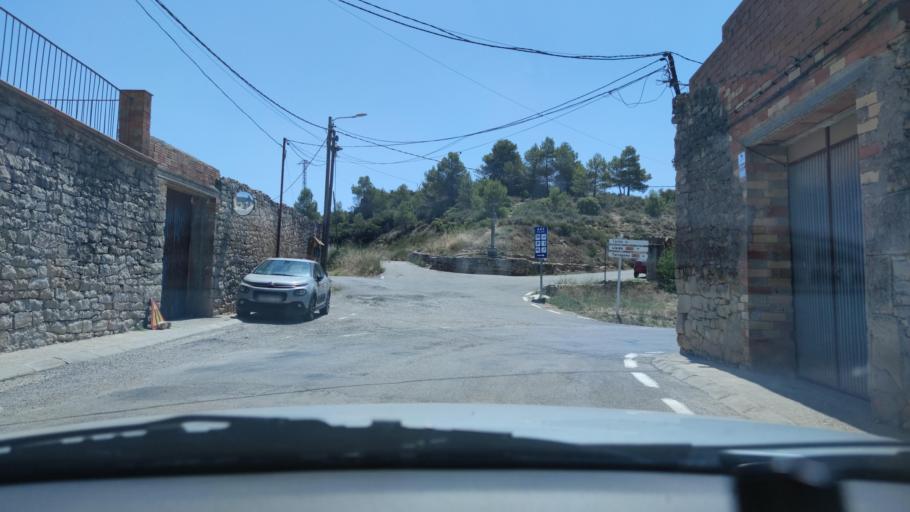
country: ES
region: Catalonia
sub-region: Provincia de Lleida
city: Fulleda
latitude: 41.4624
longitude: 1.0258
